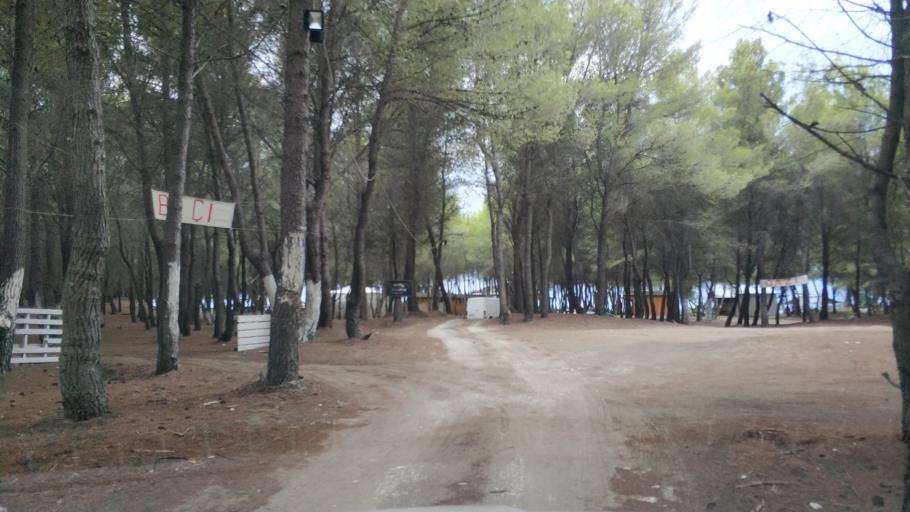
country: AL
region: Vlore
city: Vlore
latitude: 40.5022
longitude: 19.4197
